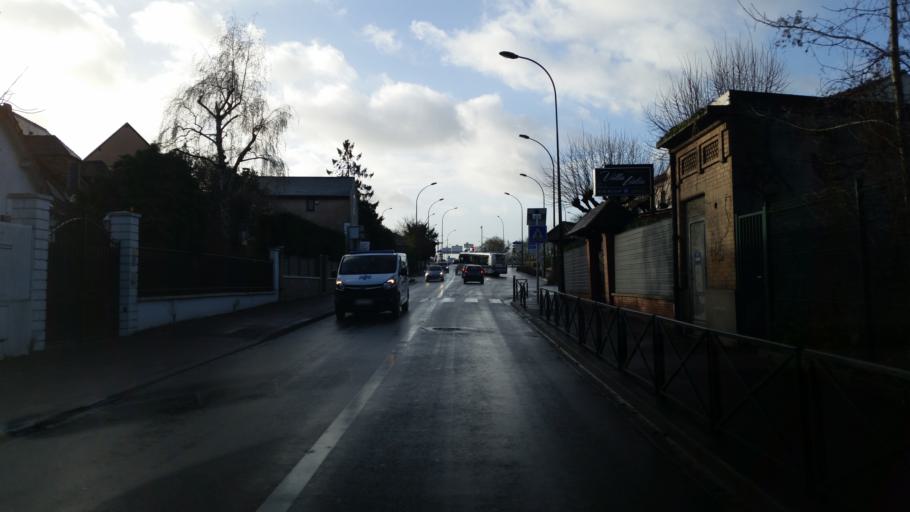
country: FR
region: Ile-de-France
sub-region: Departement des Hauts-de-Seine
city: Vaucresson
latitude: 48.8338
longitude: 2.1539
